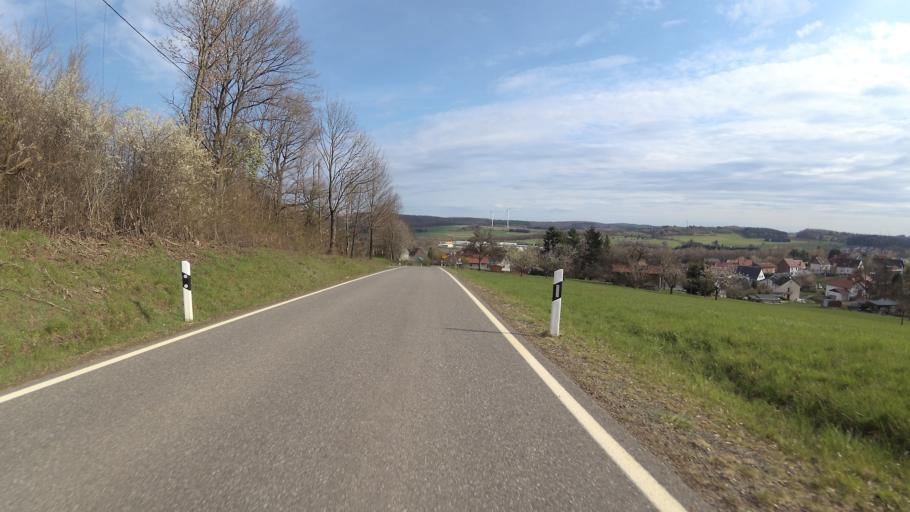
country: DE
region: Rheinland-Pfalz
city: Reichweiler
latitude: 49.5445
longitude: 7.2886
